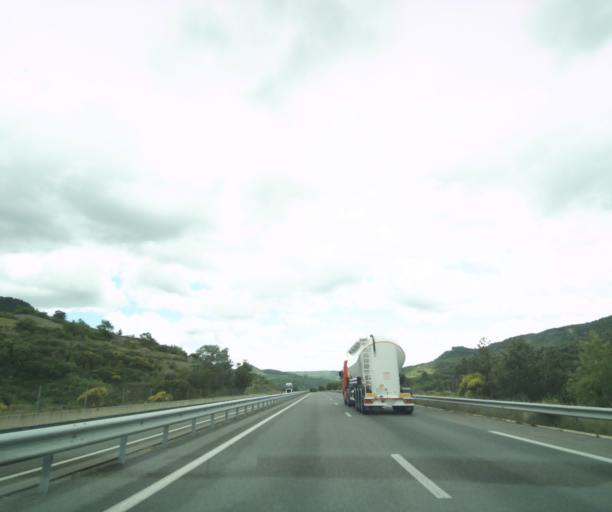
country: FR
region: Languedoc-Roussillon
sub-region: Departement de l'Herault
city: Lodeve
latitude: 43.7873
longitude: 3.3269
